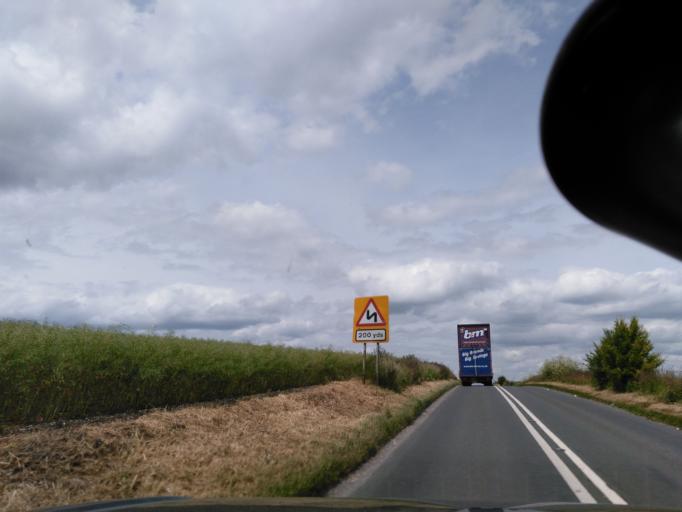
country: GB
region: England
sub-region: Wiltshire
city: Woodford
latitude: 51.1178
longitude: -1.8520
